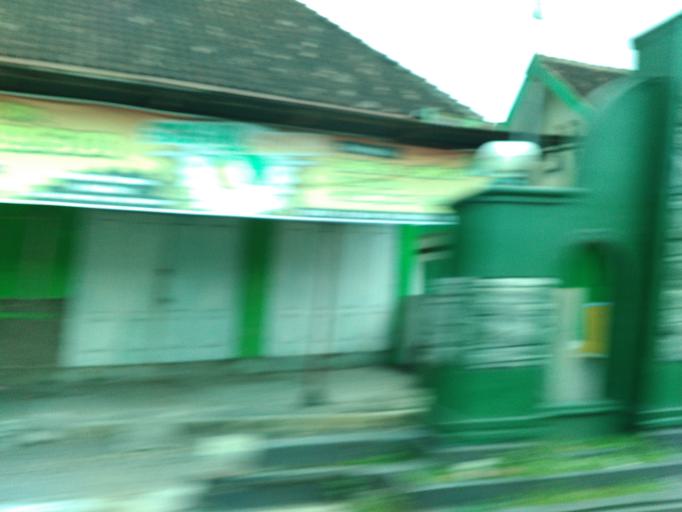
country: ID
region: Central Java
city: Delanggu
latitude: -7.6226
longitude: 110.7061
